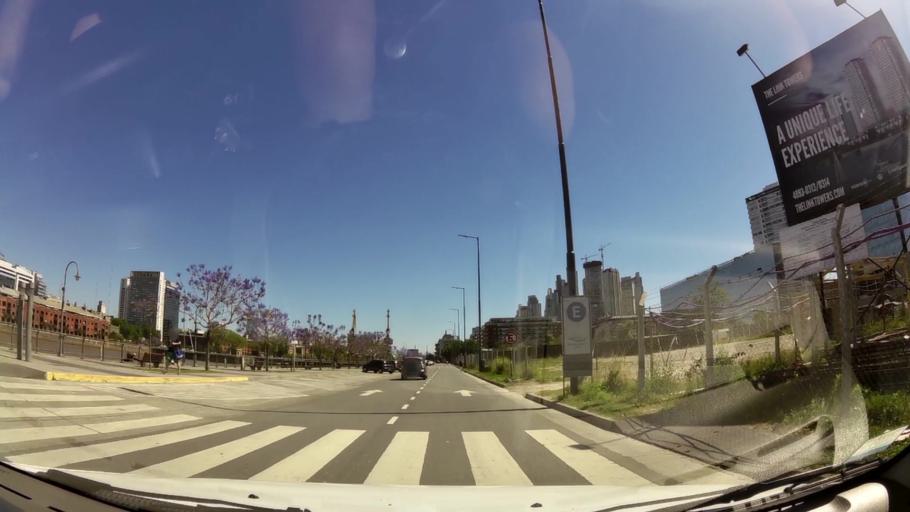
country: AR
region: Buenos Aires F.D.
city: Buenos Aires
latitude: -34.6202
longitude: -58.3627
